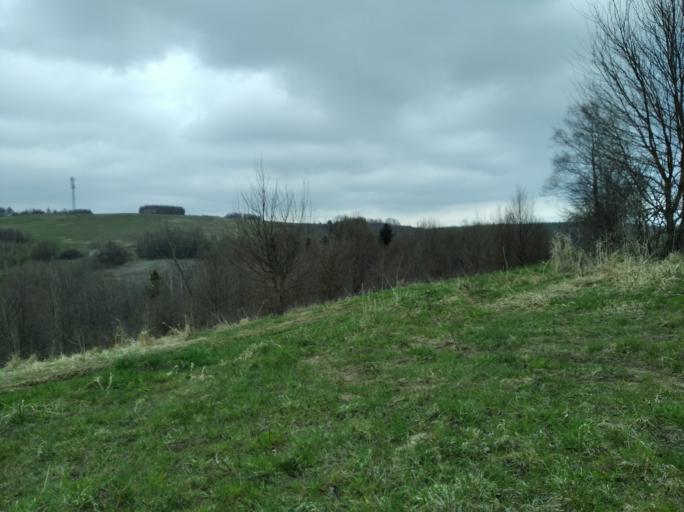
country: PL
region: Subcarpathian Voivodeship
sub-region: Powiat strzyzowski
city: Jawornik
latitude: 49.8135
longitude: 21.9002
